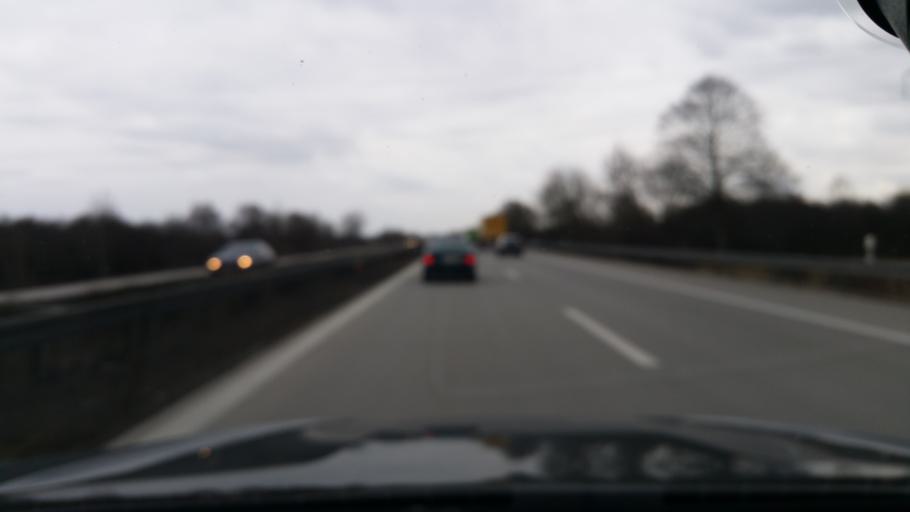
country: DE
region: Bavaria
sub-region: Upper Bavaria
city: Langenbach
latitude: 48.4004
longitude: 11.8716
